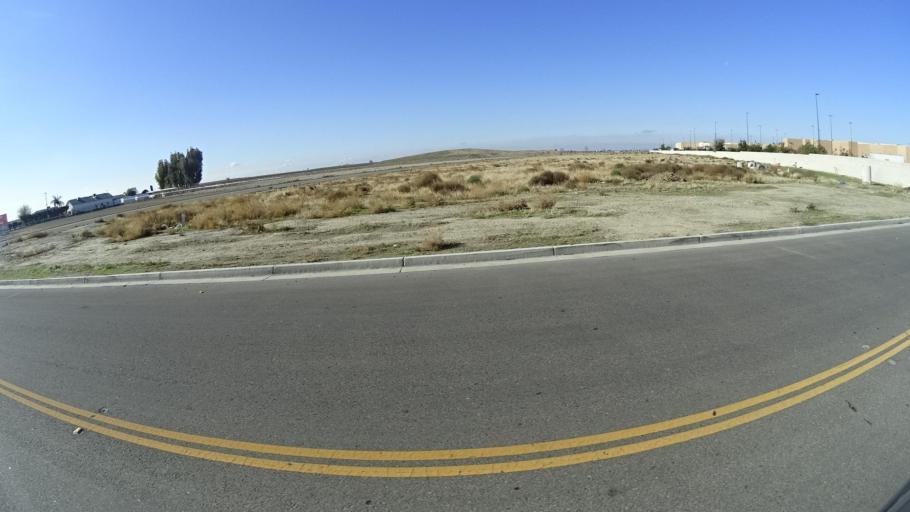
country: US
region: California
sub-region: Kern County
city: Delano
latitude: 35.7431
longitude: -119.2436
